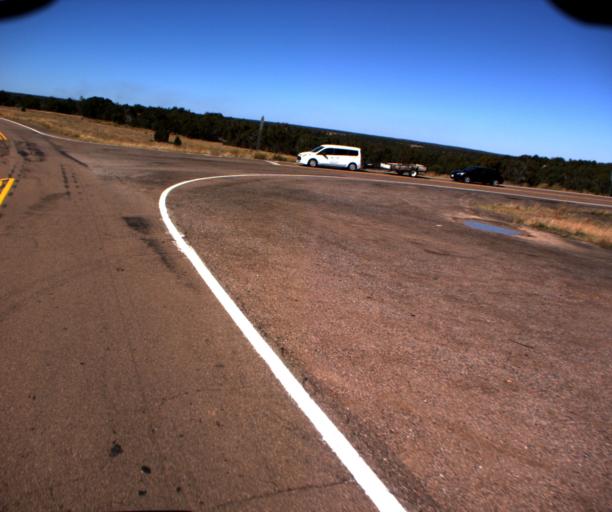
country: US
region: Arizona
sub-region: Navajo County
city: Heber-Overgaard
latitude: 34.4639
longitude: -110.4762
